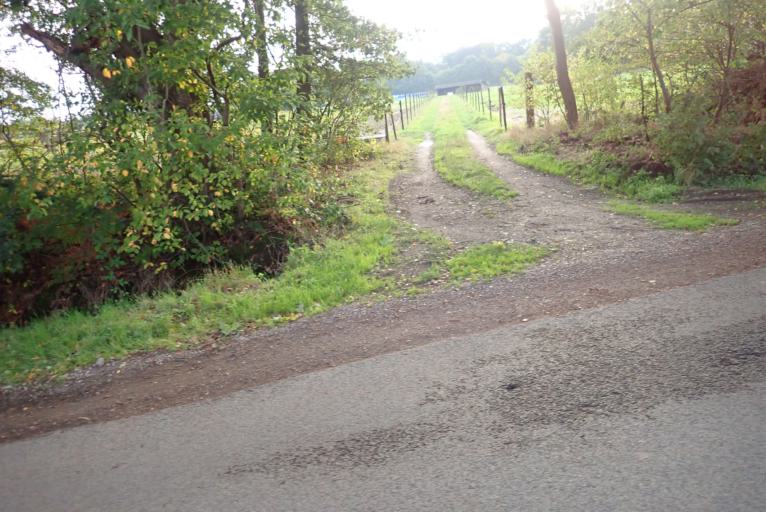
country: BE
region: Flanders
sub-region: Provincie Antwerpen
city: Zandhoven
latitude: 51.2042
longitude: 4.6395
